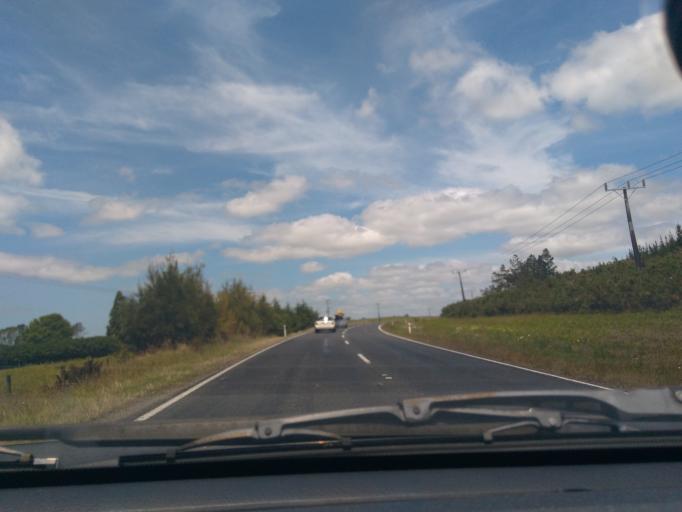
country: NZ
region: Northland
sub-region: Far North District
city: Kerikeri
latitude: -35.1220
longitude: 173.8709
